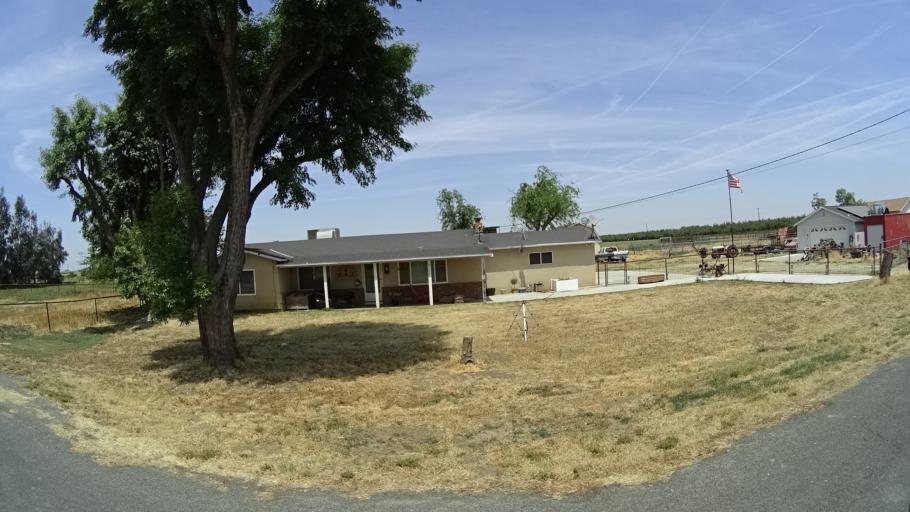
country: US
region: California
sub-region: Fresno County
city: Riverdale
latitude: 36.3947
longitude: -119.8753
